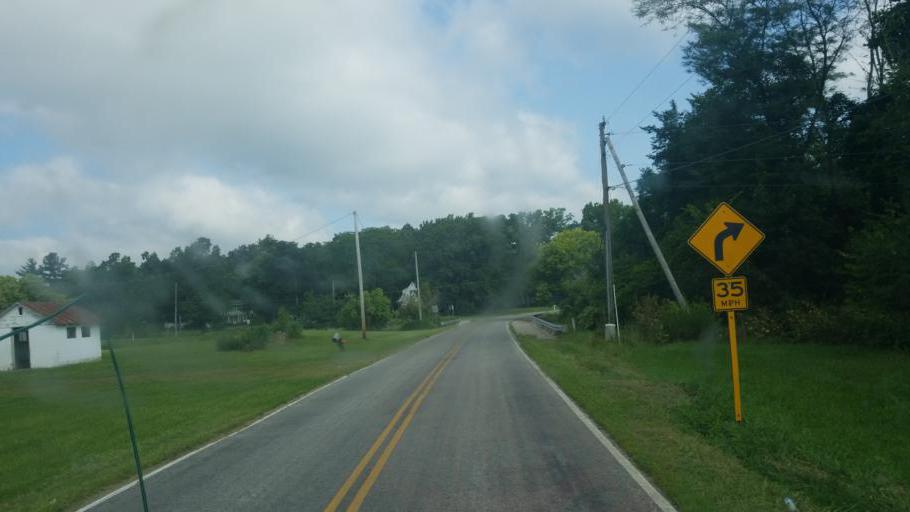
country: US
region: Ohio
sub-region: Morrow County
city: Cardington
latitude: 40.5747
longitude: -82.9981
